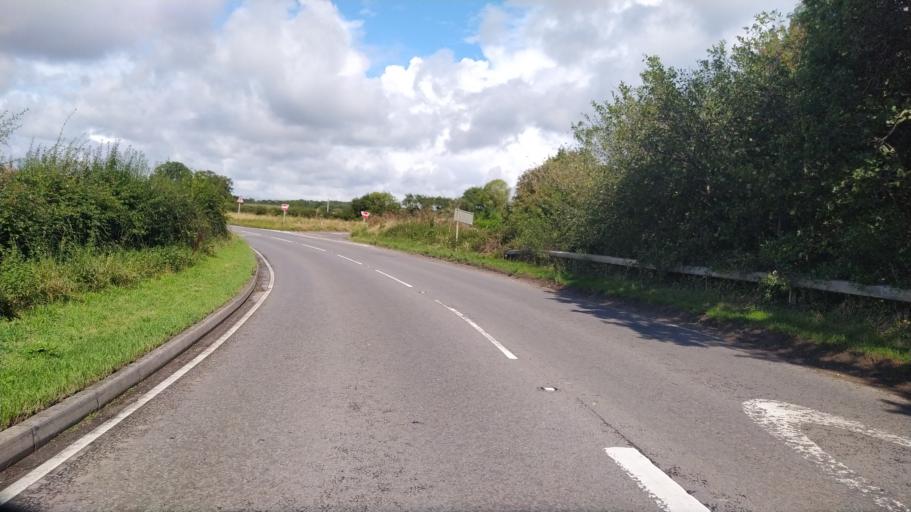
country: GB
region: England
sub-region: Dorset
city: Manston
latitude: 50.9063
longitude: -2.2533
